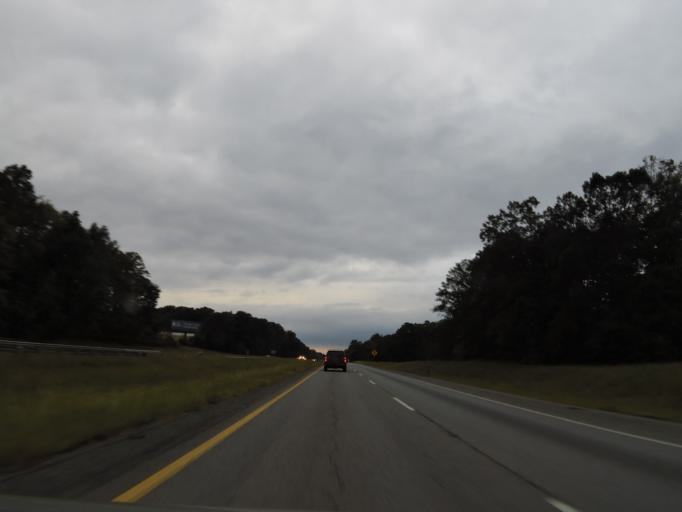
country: US
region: Alabama
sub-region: Saint Clair County
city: Ashville
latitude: 33.8625
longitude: -86.2871
